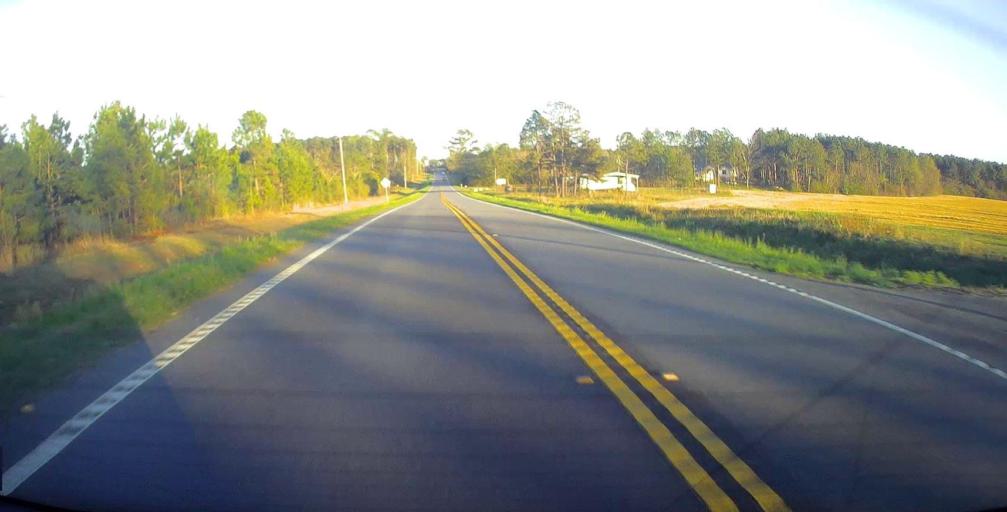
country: US
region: Georgia
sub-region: Crisp County
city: Cordele
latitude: 31.9552
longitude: -83.7269
